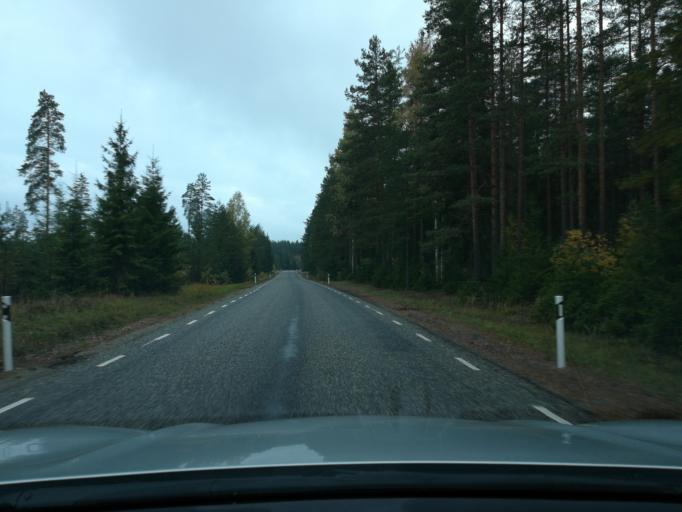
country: EE
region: Ida-Virumaa
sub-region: Johvi vald
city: Johvi
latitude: 59.1732
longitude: 27.4514
